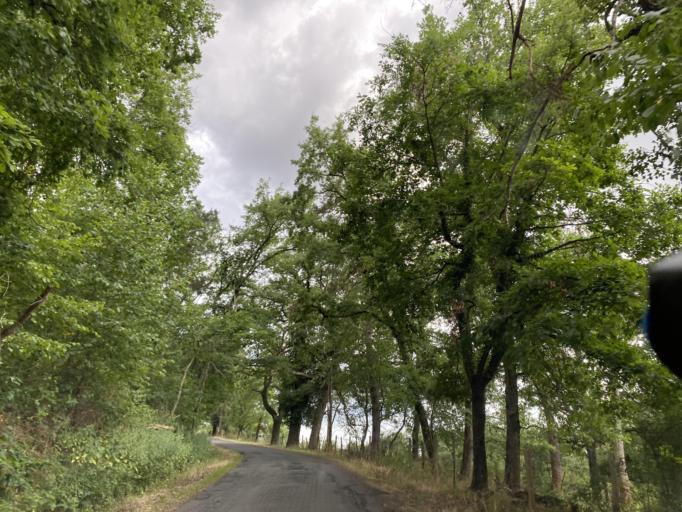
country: FR
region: Auvergne
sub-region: Departement du Puy-de-Dome
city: Peschadoires
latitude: 45.7567
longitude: 3.4519
